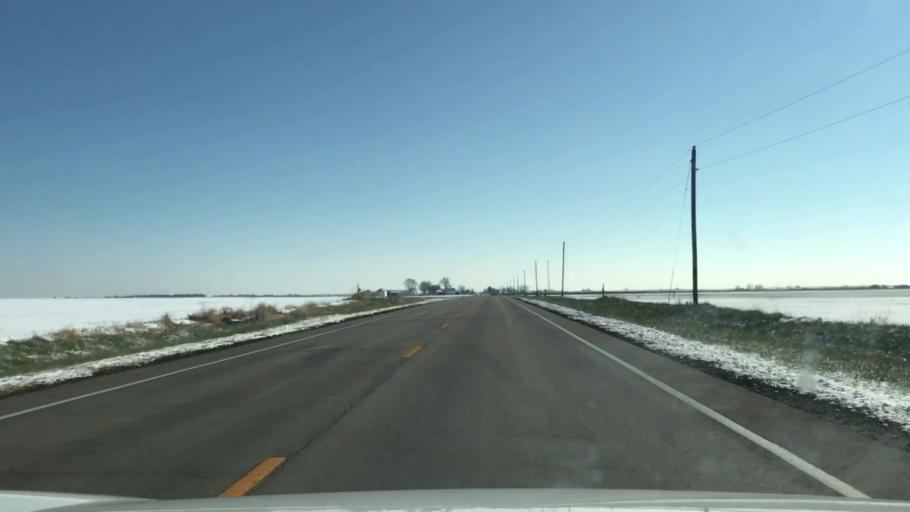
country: US
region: Illinois
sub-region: Washington County
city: Okawville
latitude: 38.4430
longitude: -89.5195
